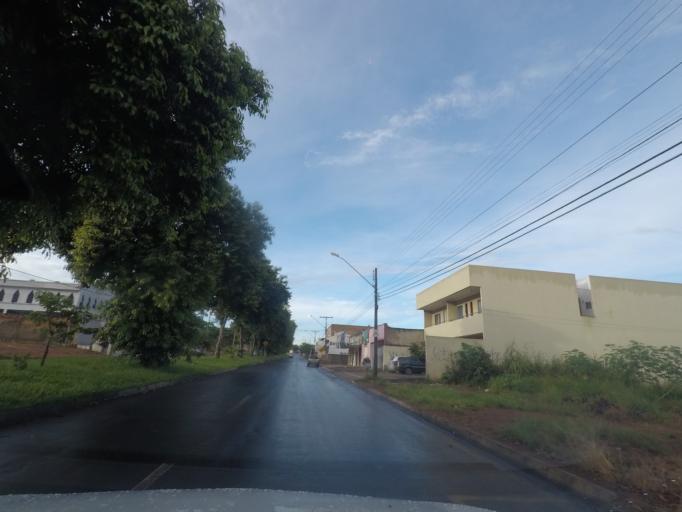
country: BR
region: Goias
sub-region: Goiania
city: Goiania
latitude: -16.7357
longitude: -49.3679
